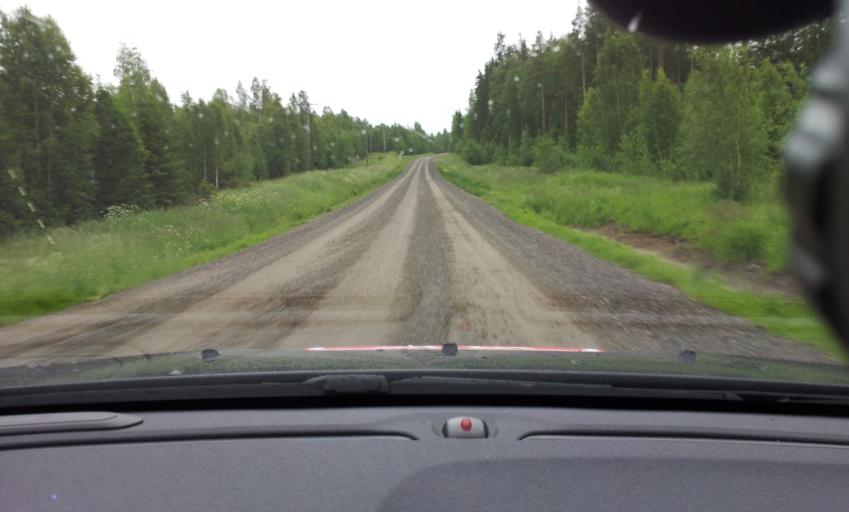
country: SE
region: Jaemtland
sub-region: Ragunda Kommun
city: Hammarstrand
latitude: 63.1279
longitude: 16.3249
